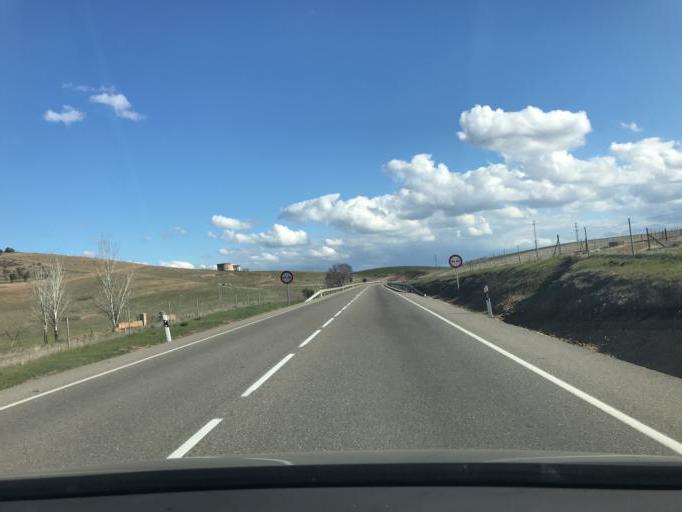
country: ES
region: Andalusia
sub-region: Province of Cordoba
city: Penarroya-Pueblonuevo
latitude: 38.3071
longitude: -5.2613
